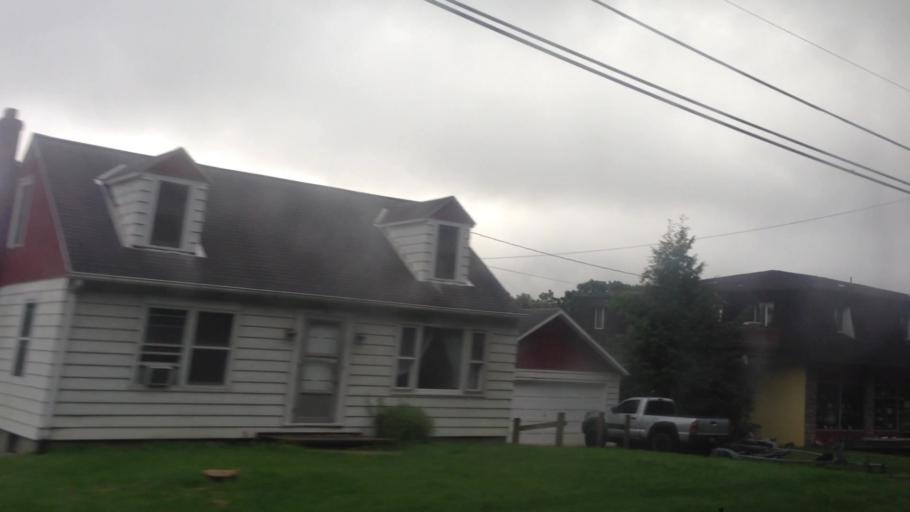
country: US
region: New York
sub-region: Ulster County
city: Lake Katrine
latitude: 41.9651
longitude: -73.9714
